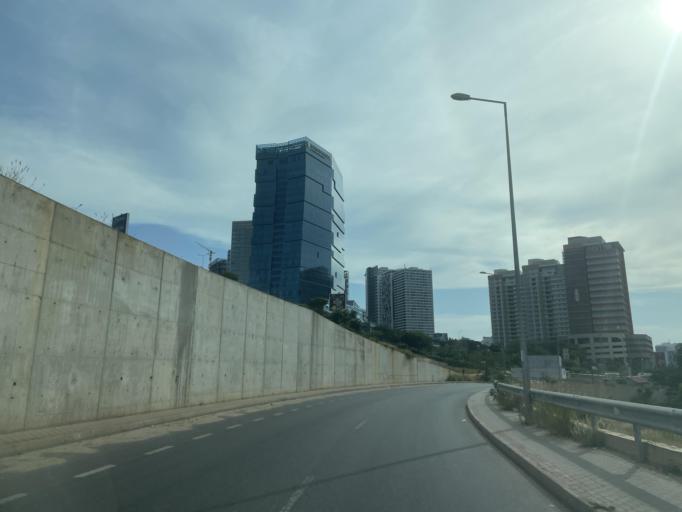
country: AO
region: Luanda
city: Luanda
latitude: -8.8095
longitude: 13.2441
